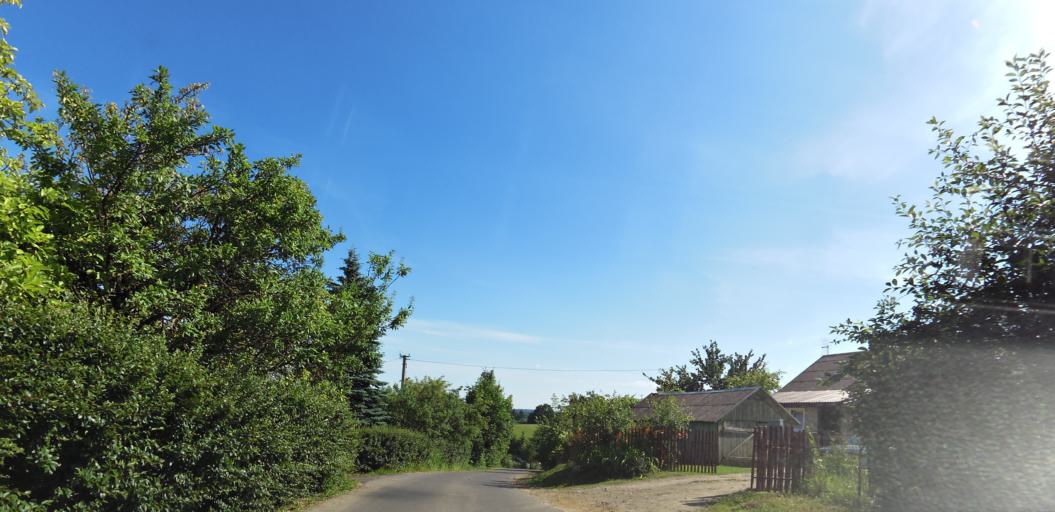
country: LT
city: Grigiskes
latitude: 54.7808
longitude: 25.0857
